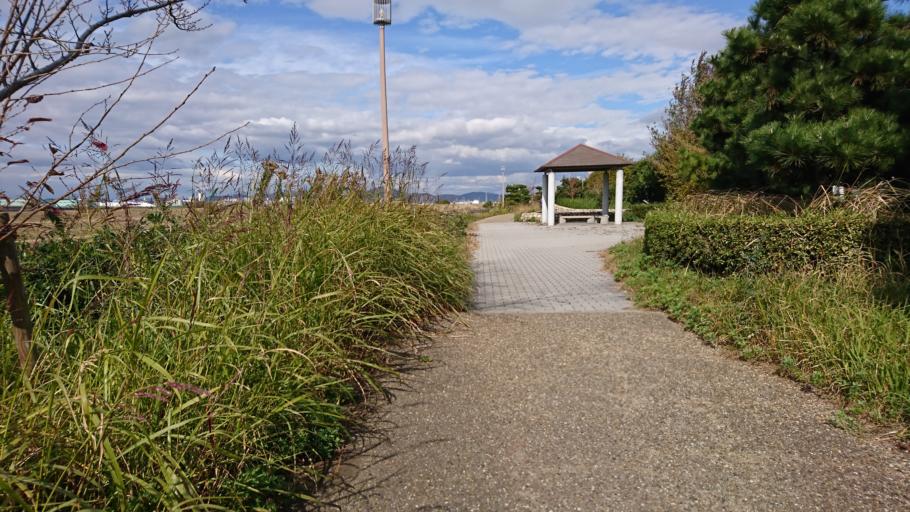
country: JP
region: Hyogo
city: Kakogawacho-honmachi
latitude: 34.7357
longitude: 134.8119
